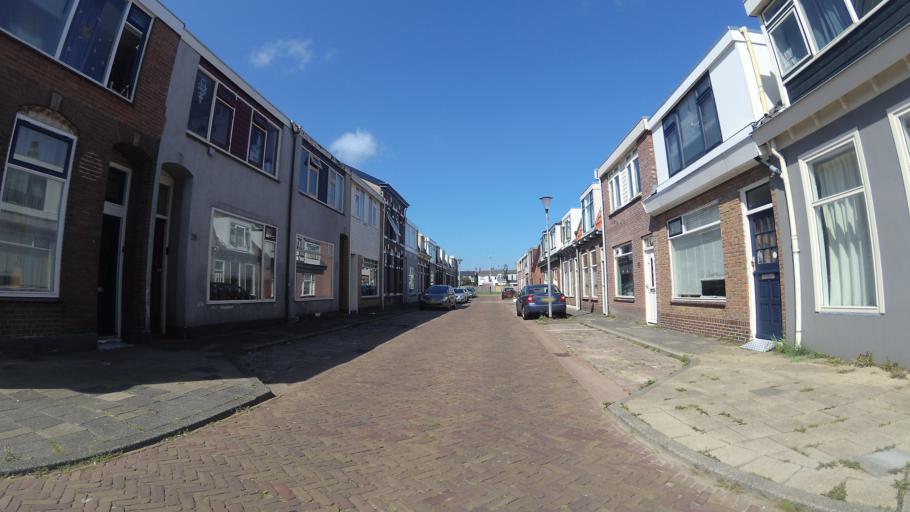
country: NL
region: North Holland
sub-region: Gemeente Den Helder
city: Den Helder
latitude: 52.9550
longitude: 4.7672
